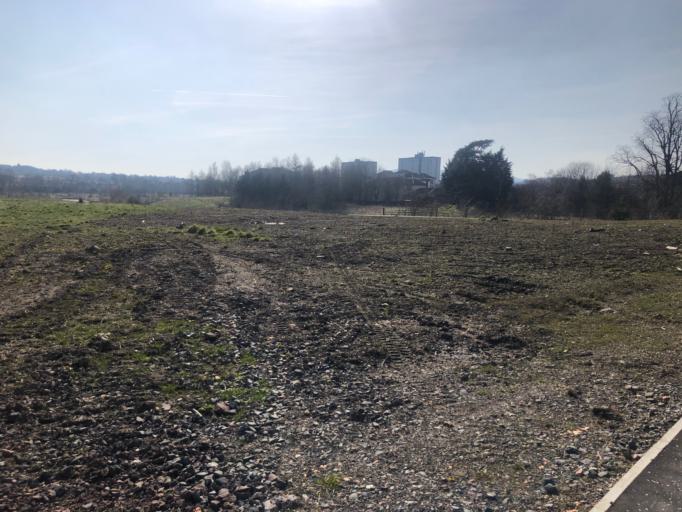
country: GB
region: Scotland
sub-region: West Lothian
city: Seafield
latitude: 55.9312
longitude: -3.1169
